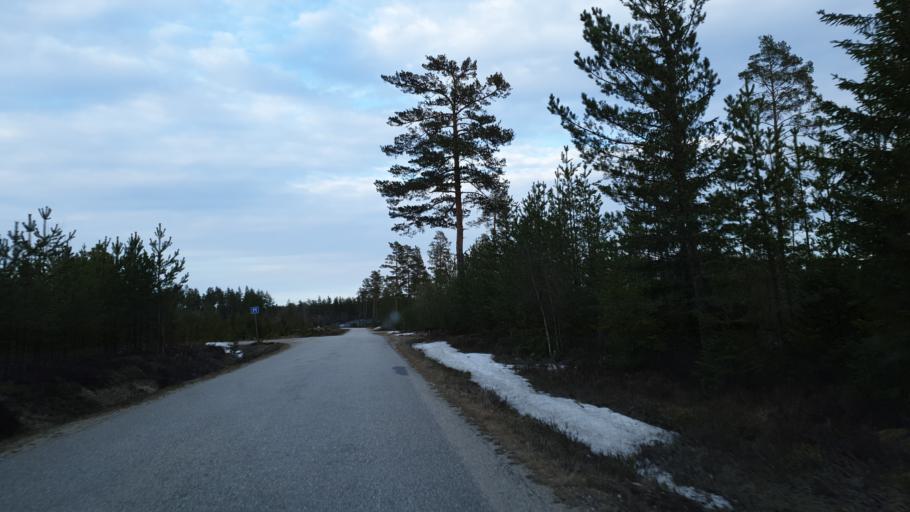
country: SE
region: Vaesternorrland
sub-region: Sundsvalls Kommun
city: Njurundabommen
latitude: 62.0308
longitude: 17.4092
